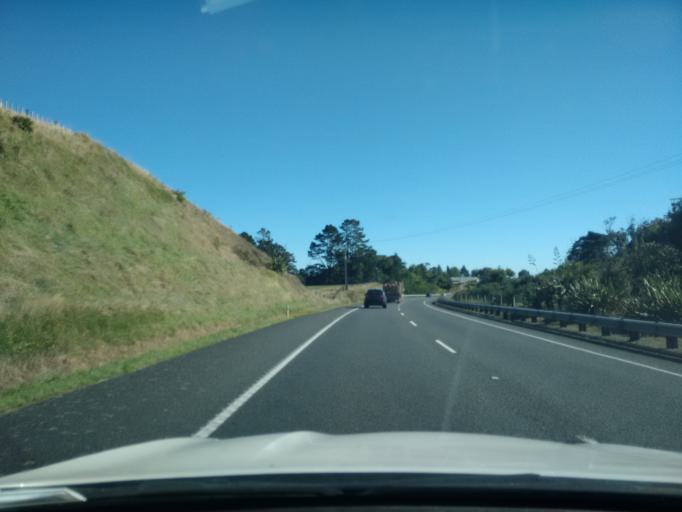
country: NZ
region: Taranaki
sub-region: New Plymouth District
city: New Plymouth
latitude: -39.1326
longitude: 174.1225
